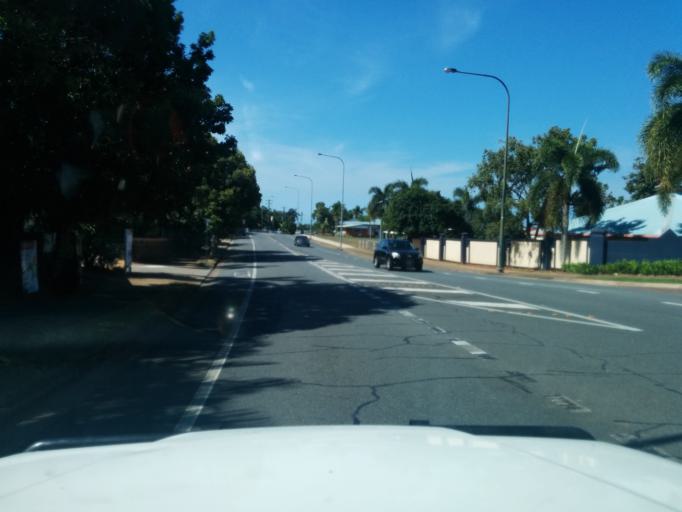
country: AU
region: Queensland
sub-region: Cairns
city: Redlynch
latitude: -16.8912
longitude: 145.6958
